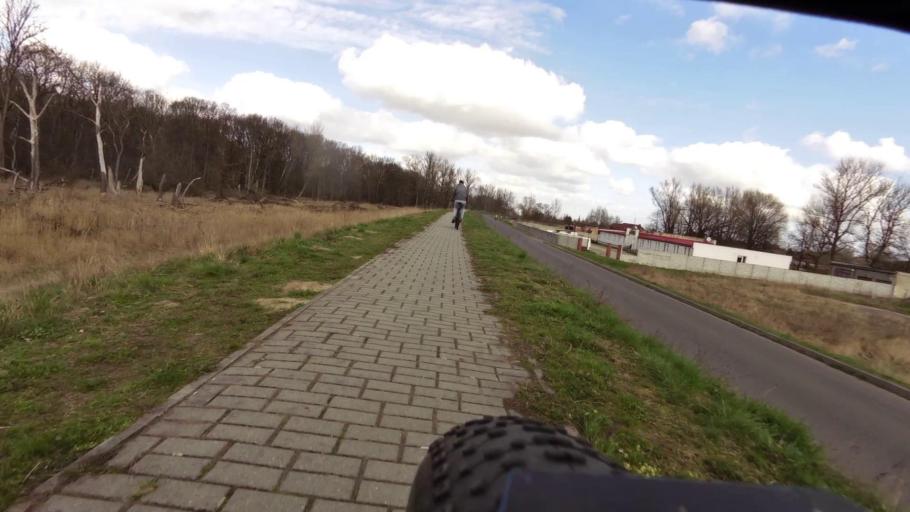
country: PL
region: Lubusz
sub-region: Powiat slubicki
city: Slubice
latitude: 52.3630
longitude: 14.5611
